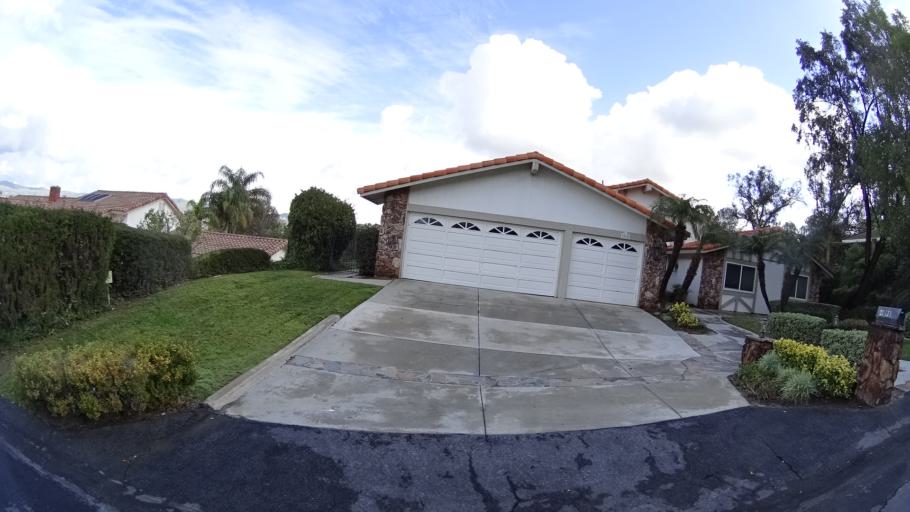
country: US
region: California
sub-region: Orange County
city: Villa Park
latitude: 33.8496
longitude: -117.7761
